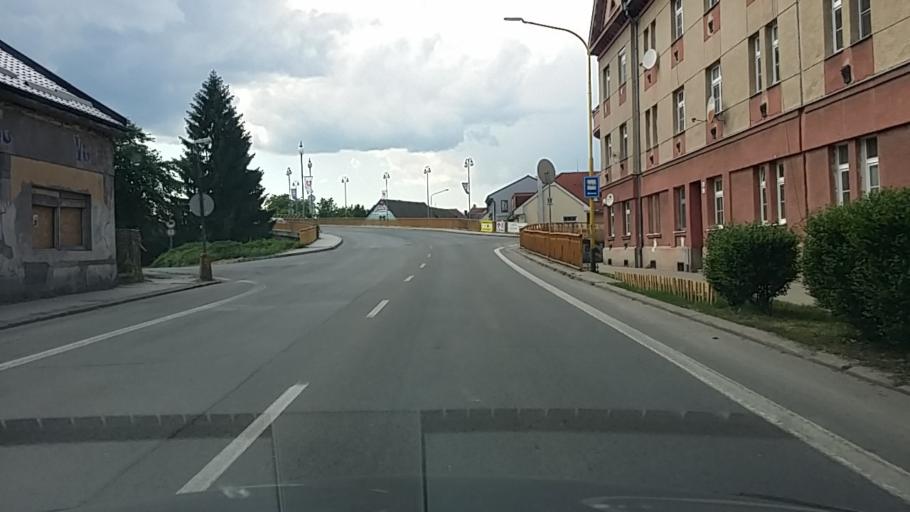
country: SK
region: Banskobystricky
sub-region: Okres Banska Bystrica
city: Zvolen
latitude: 48.5754
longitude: 19.1355
